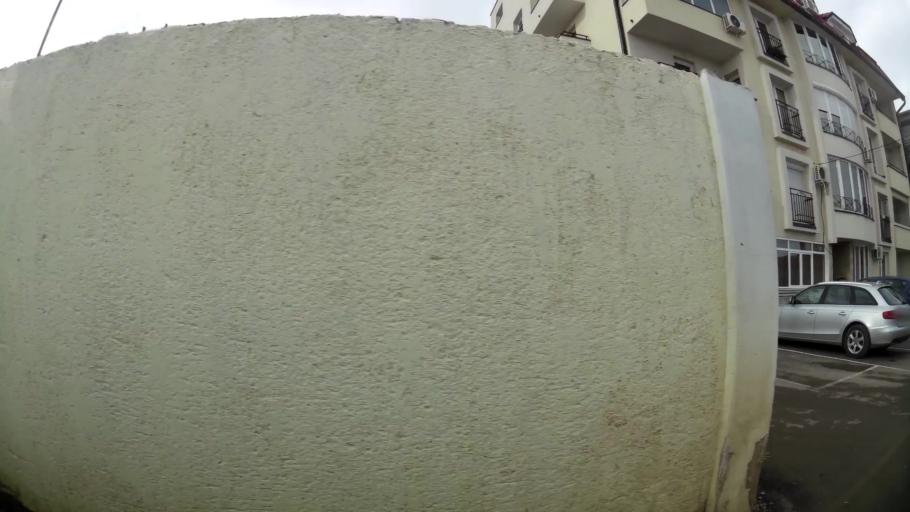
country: RS
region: Central Serbia
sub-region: Belgrade
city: Surcin
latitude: 44.8004
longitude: 20.3430
